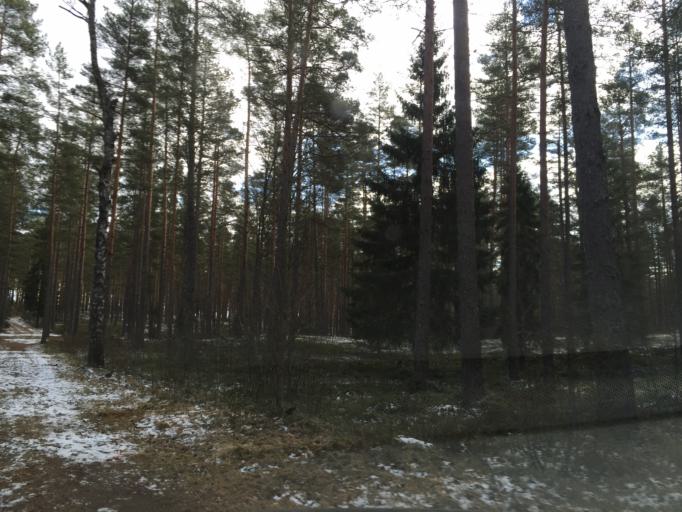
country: LV
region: Garkalne
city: Garkalne
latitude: 56.9649
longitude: 24.4373
